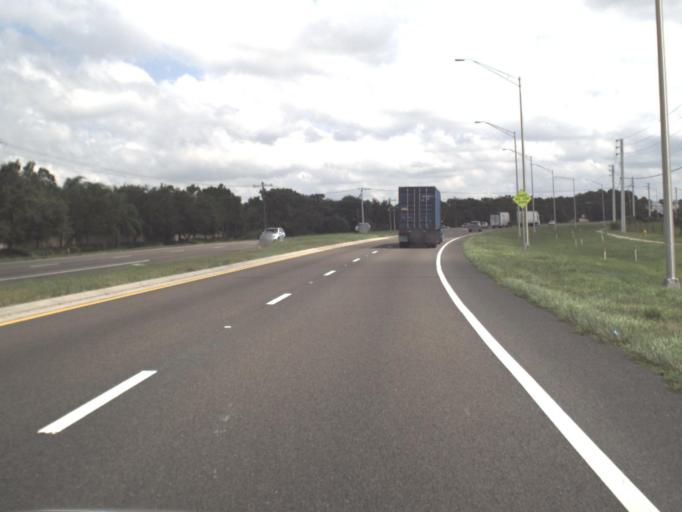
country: US
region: Florida
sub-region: Manatee County
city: Ellenton
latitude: 27.4841
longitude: -82.4118
